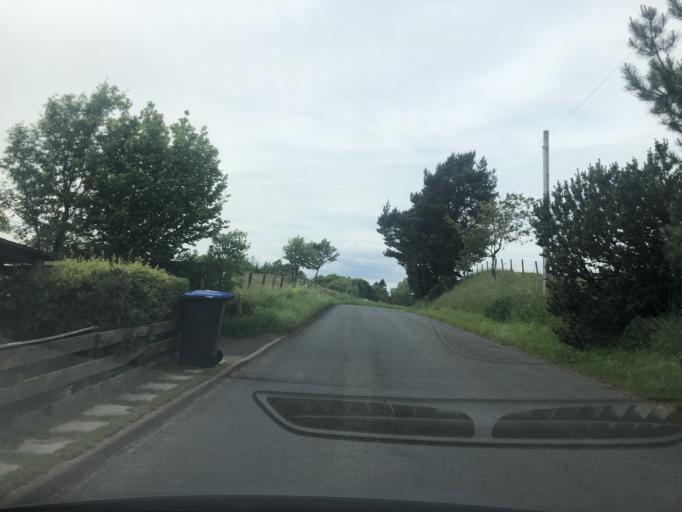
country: GB
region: Scotland
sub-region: The Scottish Borders
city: West Linton
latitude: 55.7324
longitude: -3.3277
